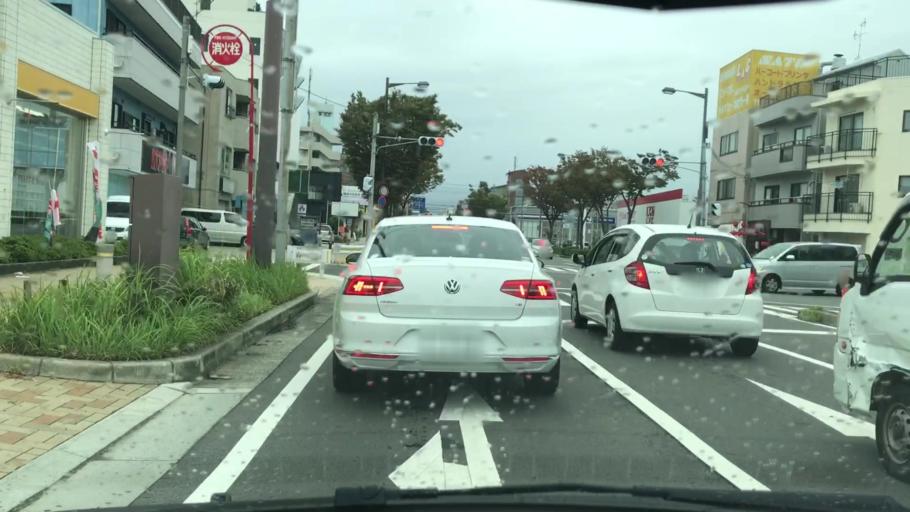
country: JP
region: Hyogo
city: Amagasaki
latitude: 34.7439
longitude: 135.4138
